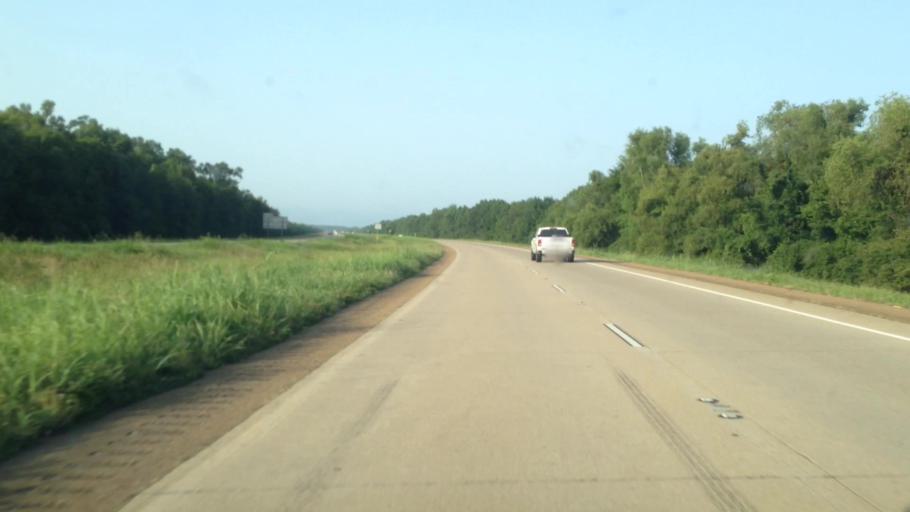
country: US
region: Louisiana
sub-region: Rapides Parish
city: Alexandria
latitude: 31.2289
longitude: -92.4647
